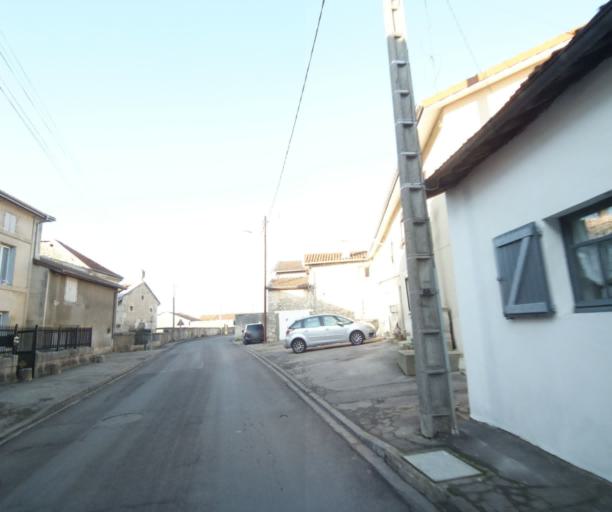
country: FR
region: Champagne-Ardenne
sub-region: Departement de la Haute-Marne
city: Bienville
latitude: 48.5730
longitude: 5.0454
